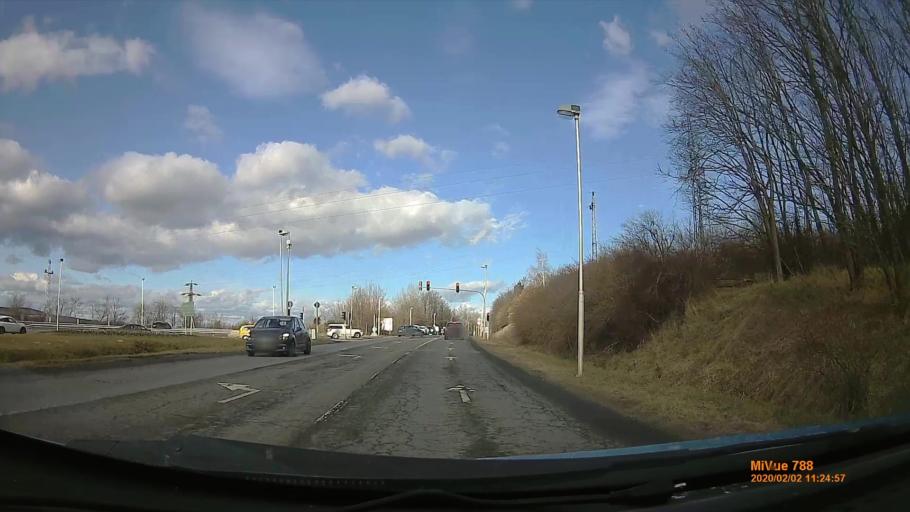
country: HU
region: Gyor-Moson-Sopron
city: Sopron
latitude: 47.6990
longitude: 16.5802
